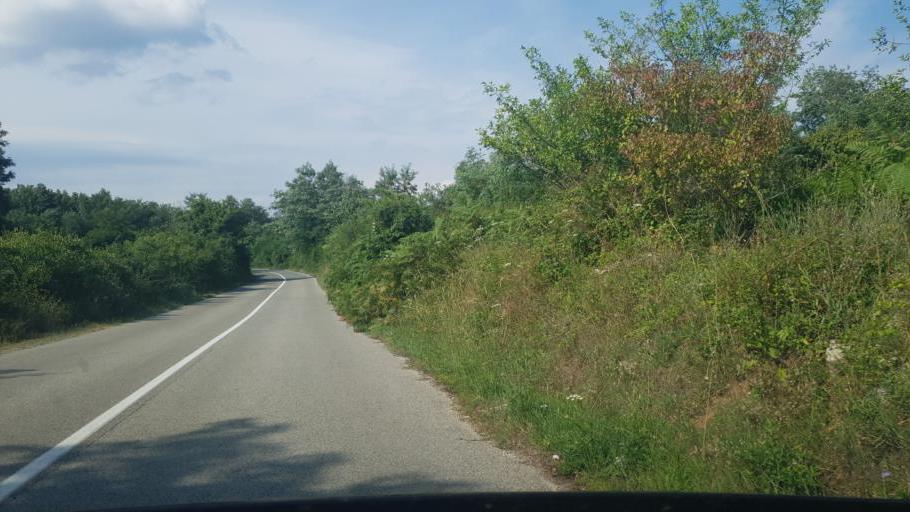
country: HR
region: Primorsko-Goranska
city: Punat
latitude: 45.0999
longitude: 14.6414
